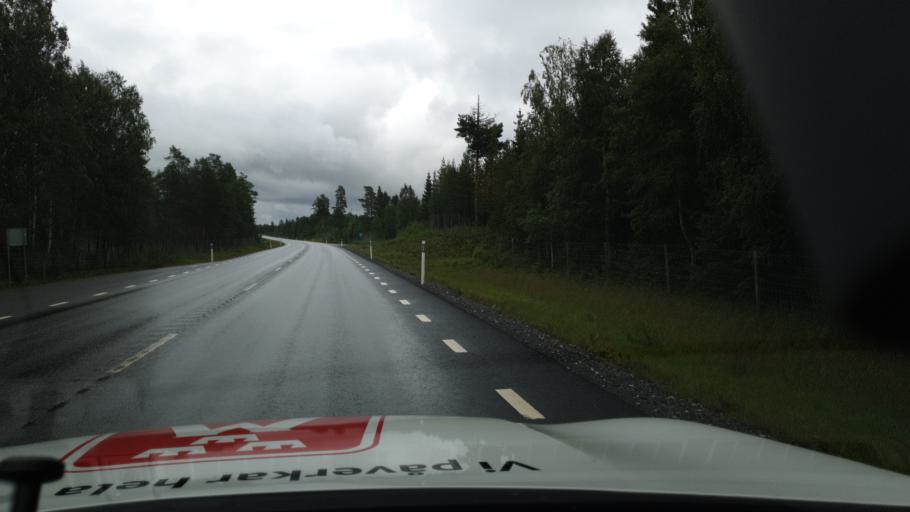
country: SE
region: Vaesterbotten
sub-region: Skelleftea Kommun
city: Forsbacka
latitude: 64.8308
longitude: 20.5478
